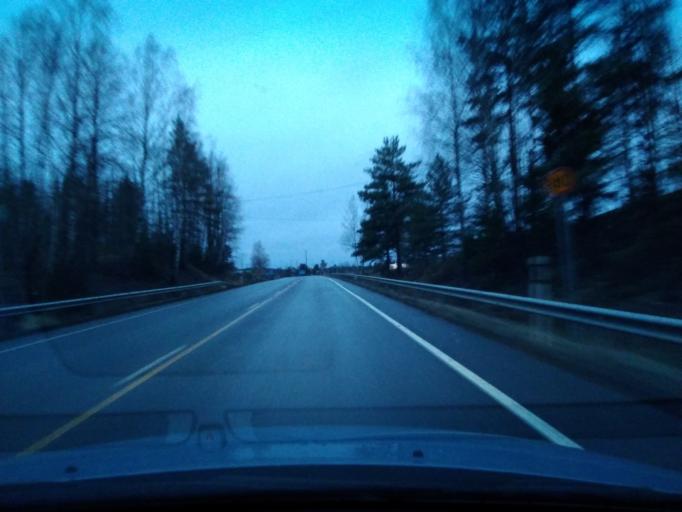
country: FI
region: Uusimaa
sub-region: Porvoo
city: Askola
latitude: 60.4919
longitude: 25.5560
